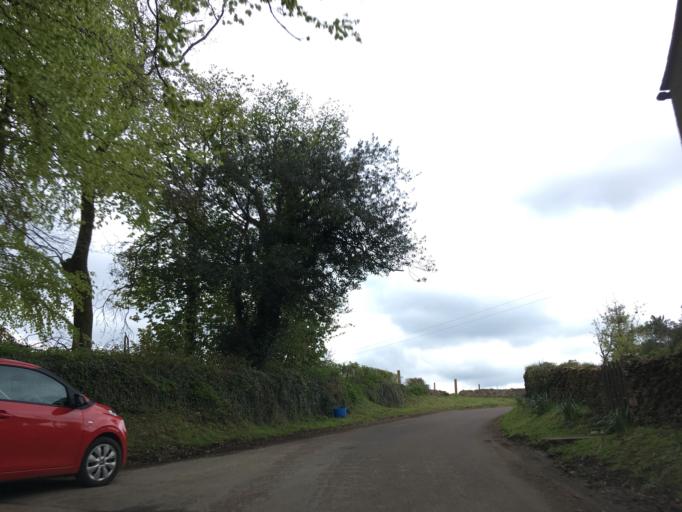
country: GB
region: England
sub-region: Gloucestershire
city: Wotton-under-Edge
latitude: 51.6441
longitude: -2.3053
